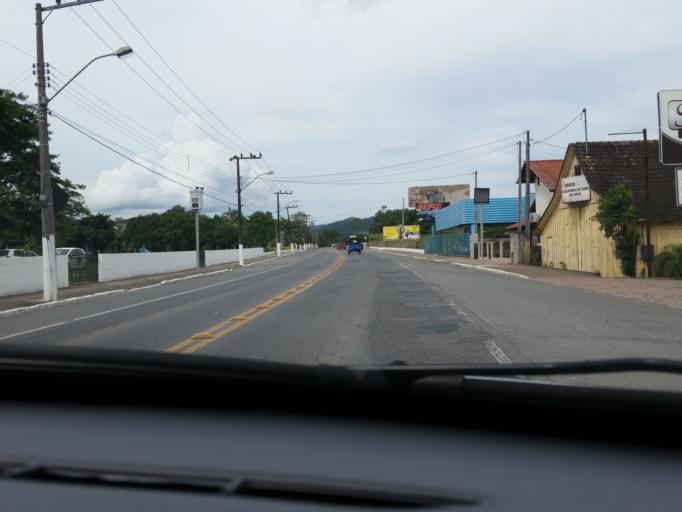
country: BR
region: Santa Catarina
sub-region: Rodeio
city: Gavea
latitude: -27.0315
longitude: -49.3842
